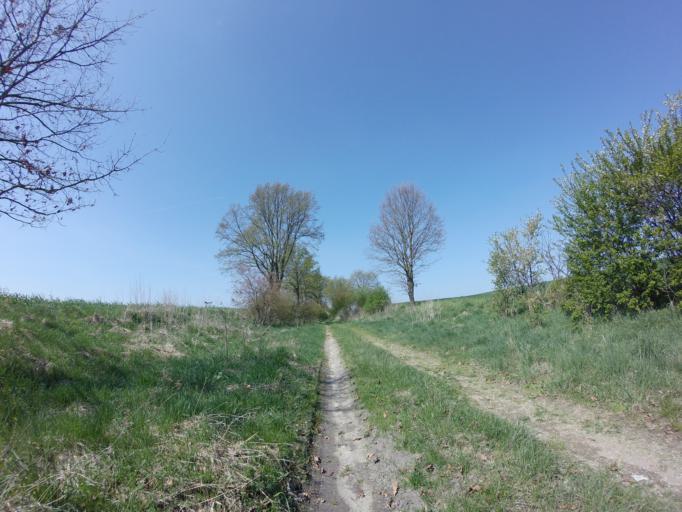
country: PL
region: West Pomeranian Voivodeship
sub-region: Powiat choszczenski
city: Choszczno
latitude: 53.1885
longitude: 15.3872
